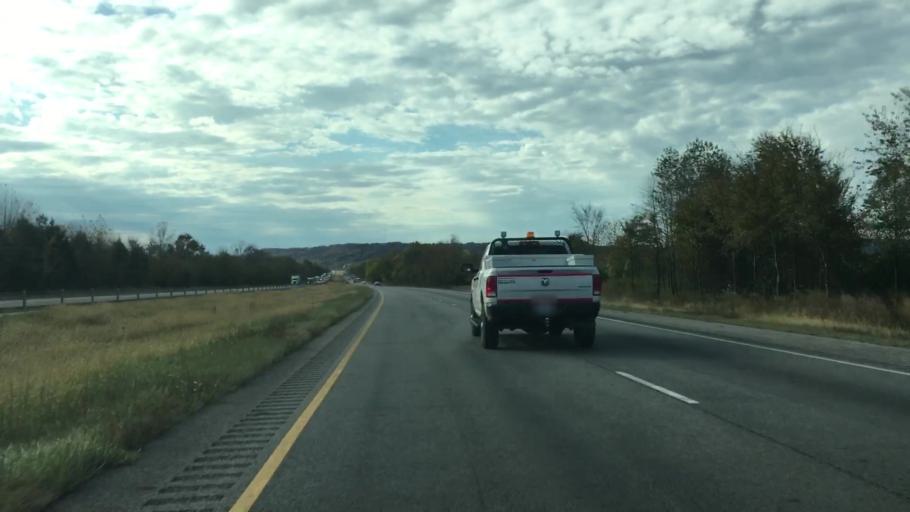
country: US
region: Arkansas
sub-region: Pope County
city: Atkins
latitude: 35.2516
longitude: -92.8941
